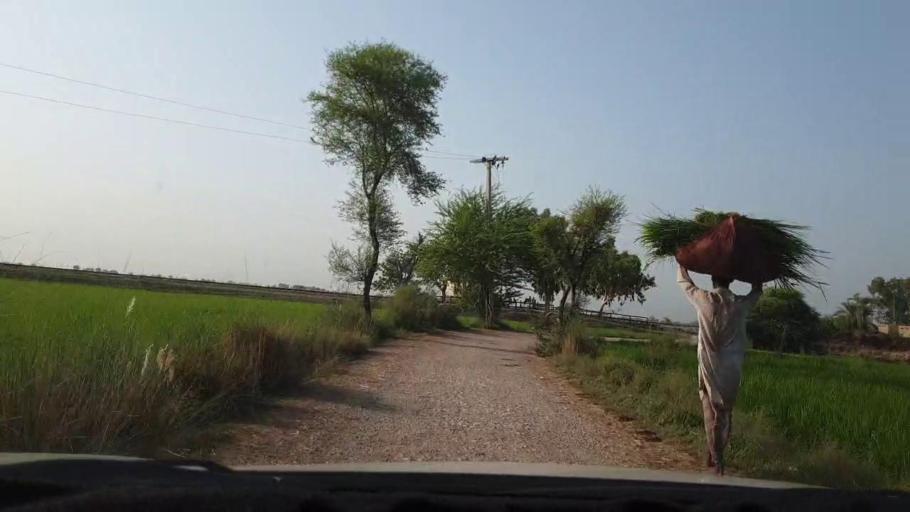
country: PK
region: Sindh
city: Larkana
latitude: 27.5030
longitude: 68.1753
